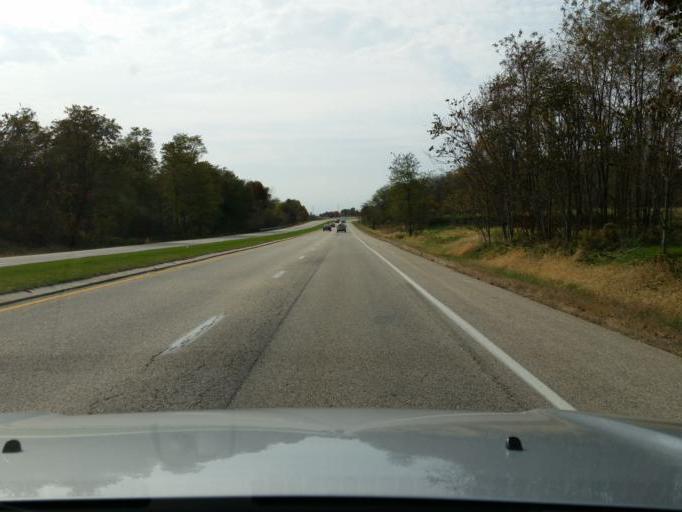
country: US
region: Pennsylvania
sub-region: Dauphin County
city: Palmdale
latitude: 40.3038
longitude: -76.6279
